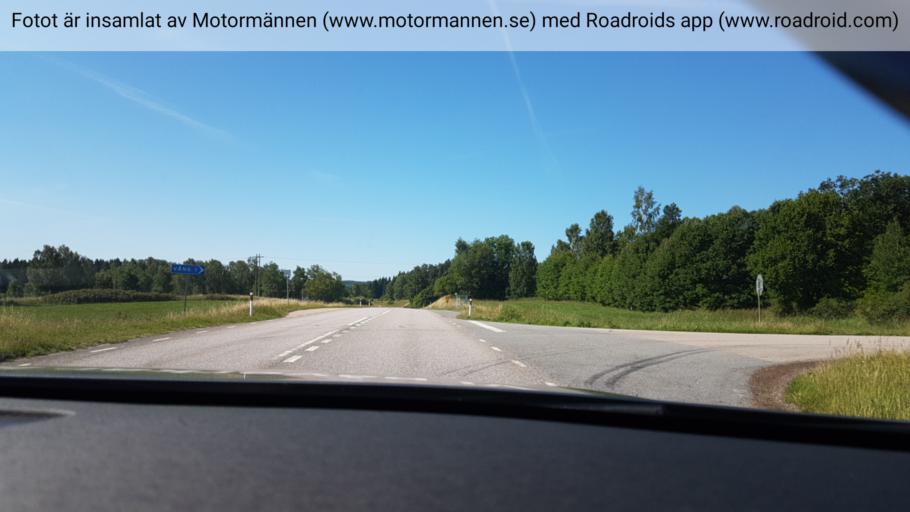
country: SE
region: Vaestra Goetaland
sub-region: Ulricehamns Kommun
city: Ulricehamn
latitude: 57.8880
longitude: 13.4354
